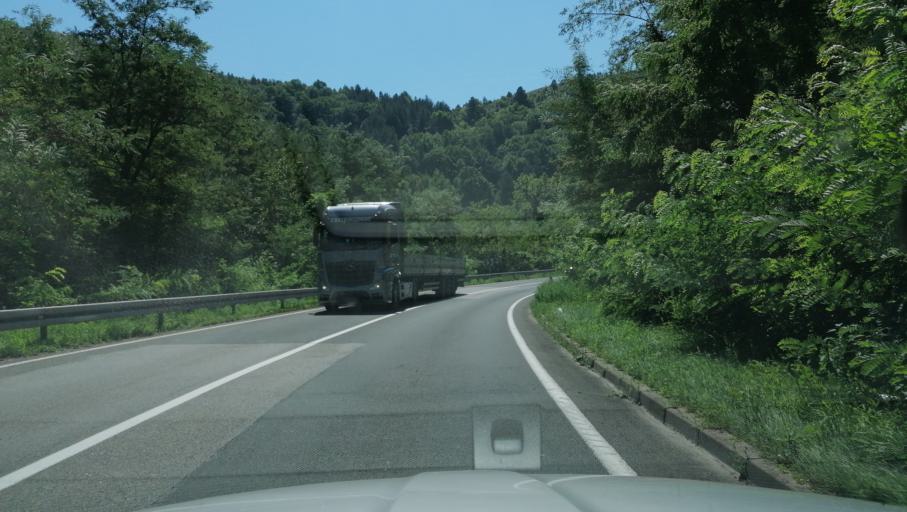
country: RS
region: Central Serbia
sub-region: Raski Okrug
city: Kraljevo
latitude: 43.6177
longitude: 20.5541
